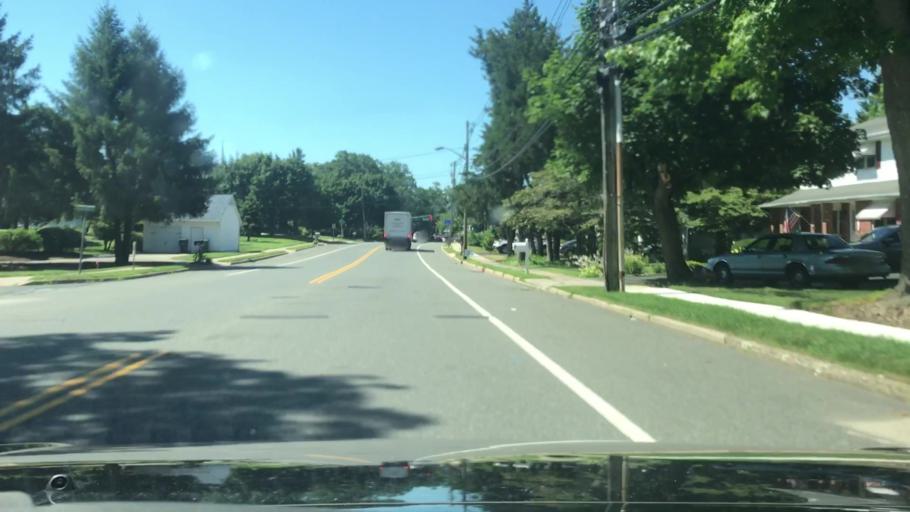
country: US
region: New Jersey
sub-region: Ocean County
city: Toms River
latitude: 39.9747
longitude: -74.1989
